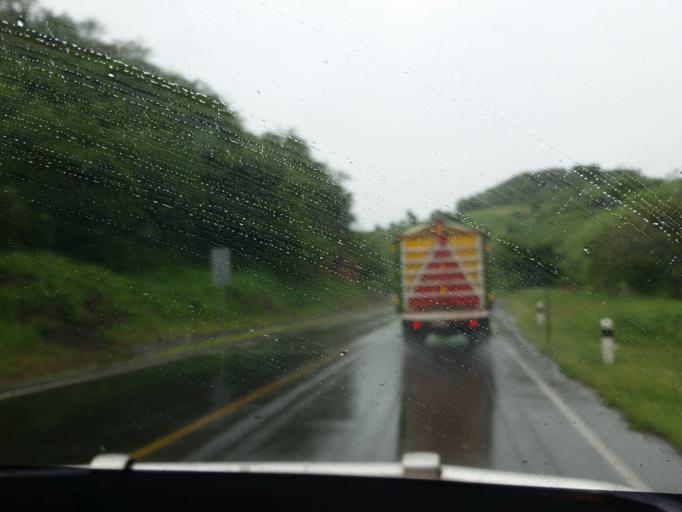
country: NI
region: Matagalpa
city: Matagalpa
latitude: 12.8862
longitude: -86.0565
